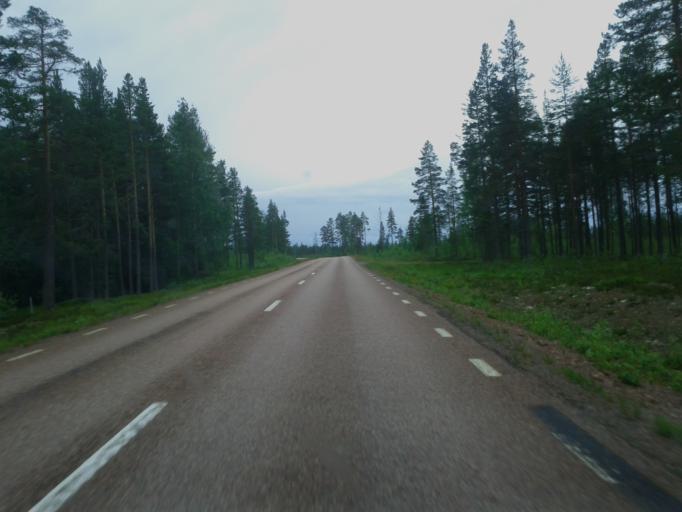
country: SE
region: Dalarna
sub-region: Alvdalens Kommun
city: AElvdalen
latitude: 61.4713
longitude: 13.4228
